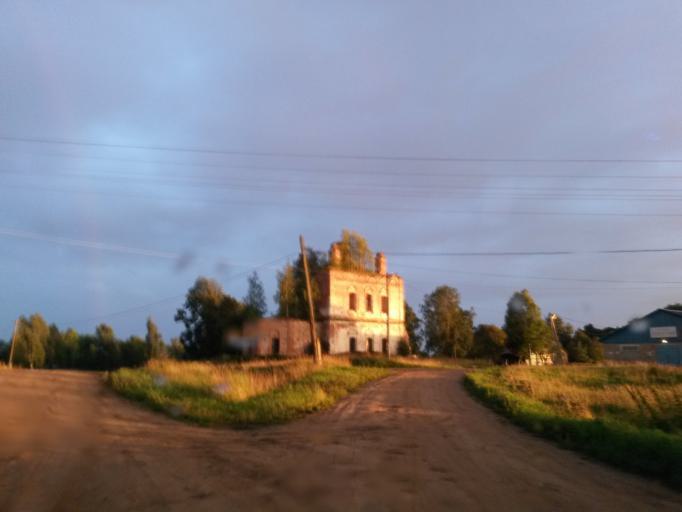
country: RU
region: Jaroslavl
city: Gavrilov-Yam
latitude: 57.3092
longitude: 39.9470
